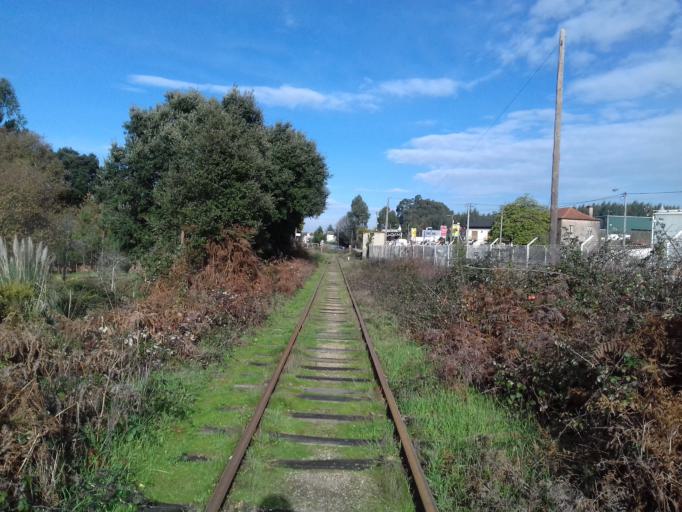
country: PT
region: Aveiro
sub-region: Albergaria-A-Velha
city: Branca
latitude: 40.7674
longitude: -8.4830
